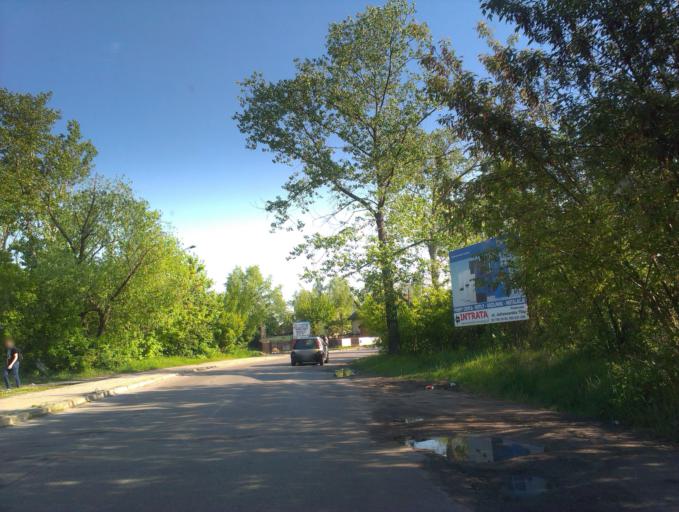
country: PL
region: Masovian Voivodeship
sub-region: Powiat piaseczynski
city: Piaseczno
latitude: 52.0767
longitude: 21.0362
